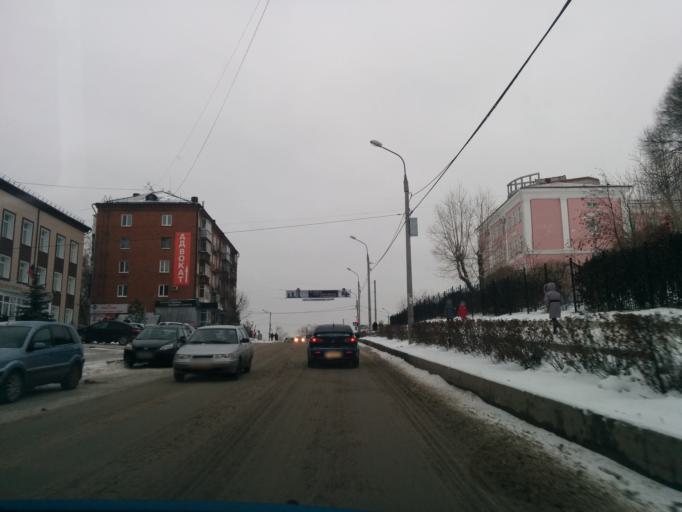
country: RU
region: Perm
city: Perm
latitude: 58.0042
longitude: 56.2068
